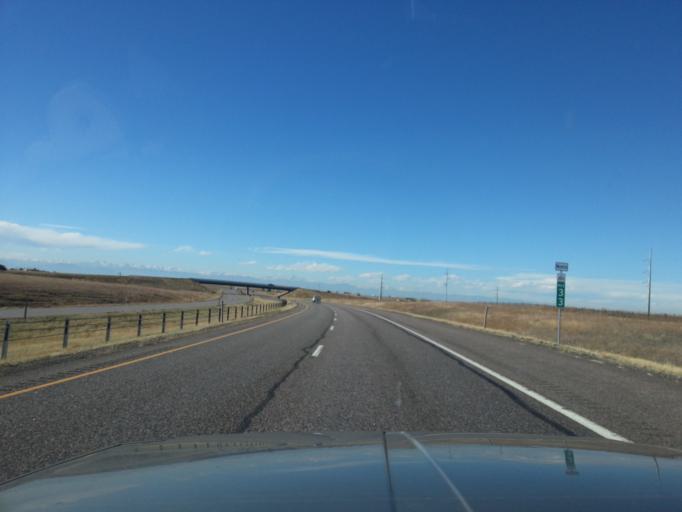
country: US
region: Colorado
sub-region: Adams County
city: Brighton
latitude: 39.9043
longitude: -104.7664
